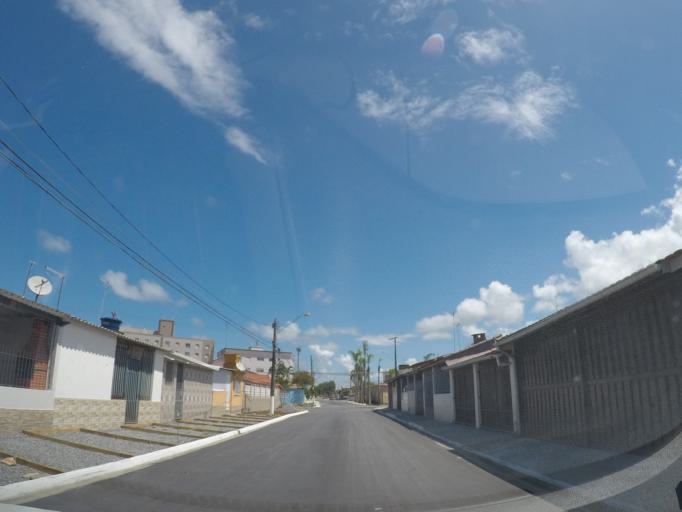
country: BR
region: Sao Paulo
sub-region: Mongagua
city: Mongagua
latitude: -24.0636
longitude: -46.5588
